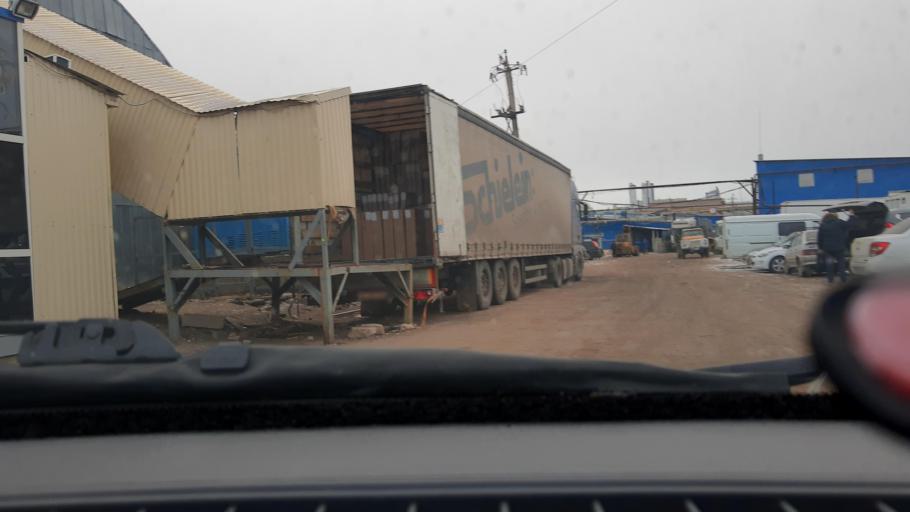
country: RU
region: Bashkortostan
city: Ufa
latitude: 54.7501
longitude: 55.9128
